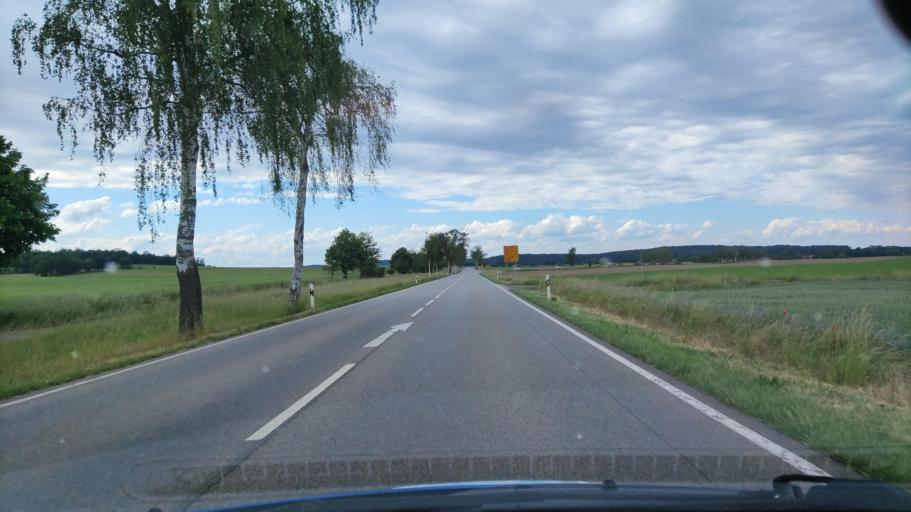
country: DE
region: Saxony-Anhalt
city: Gardelegen
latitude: 52.5873
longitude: 11.3468
